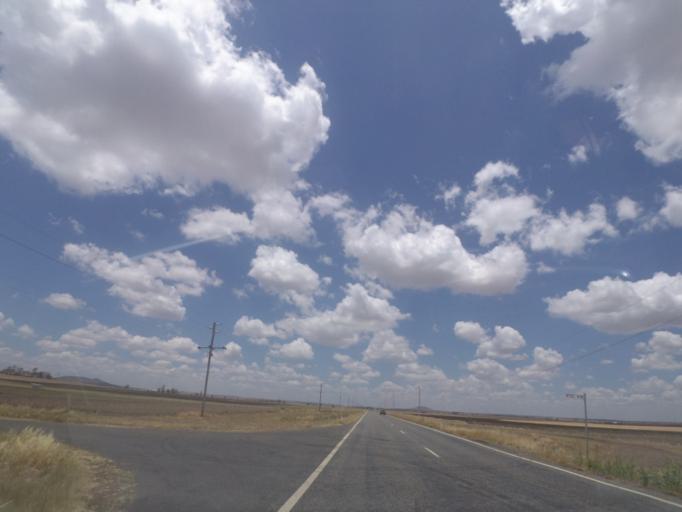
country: AU
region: Queensland
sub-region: Toowoomba
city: Top Camp
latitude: -27.8977
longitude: 151.9753
